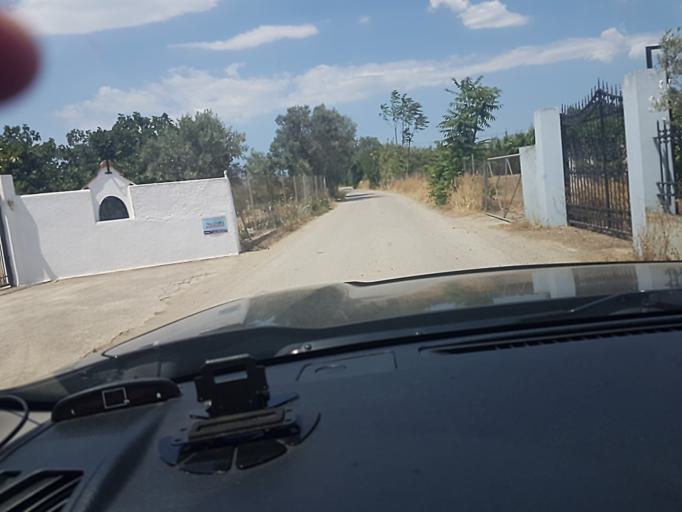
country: GR
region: Central Greece
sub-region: Nomos Evvoias
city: Ayios Nikolaos
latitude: 38.4140
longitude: 23.6598
